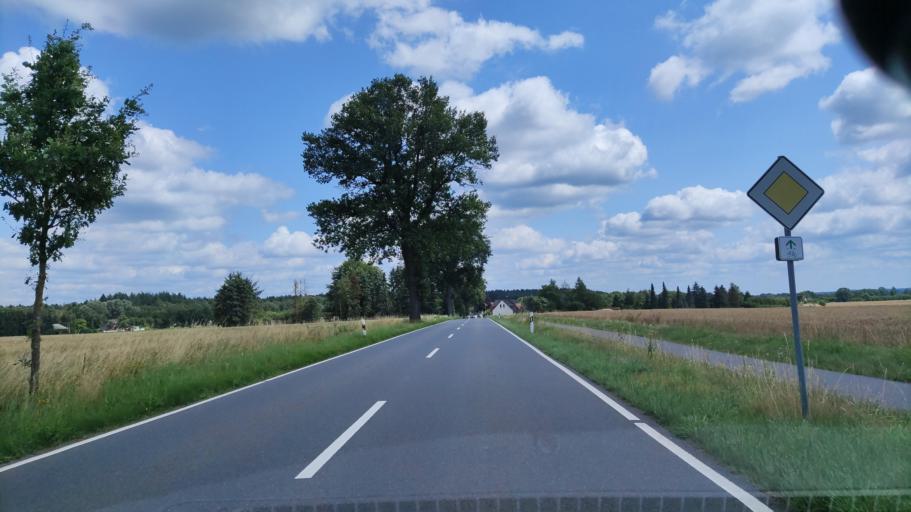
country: DE
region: Lower Saxony
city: Walsrode
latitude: 52.9078
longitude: 9.5921
